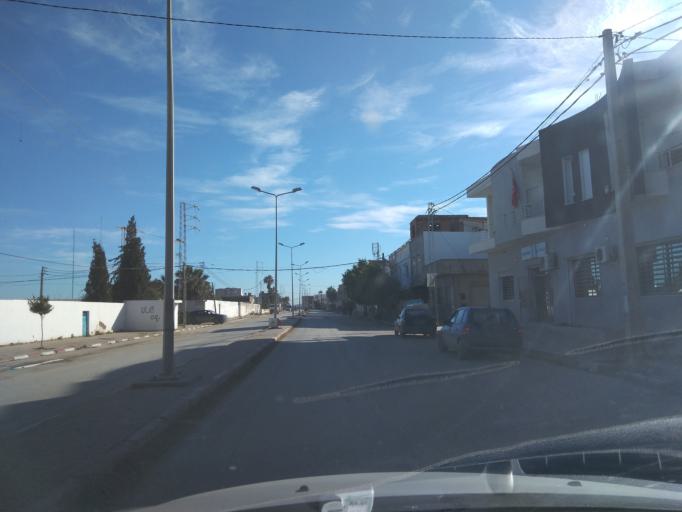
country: TN
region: Ariana
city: Qal'at al Andalus
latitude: 37.0580
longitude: 10.1200
